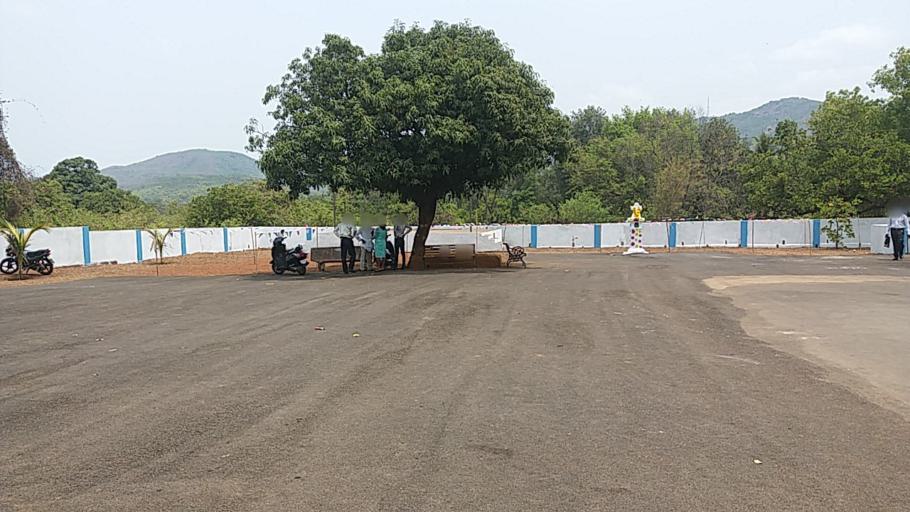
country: IN
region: Goa
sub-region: South Goa
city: Cuncolim
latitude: 15.1872
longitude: 74.0360
